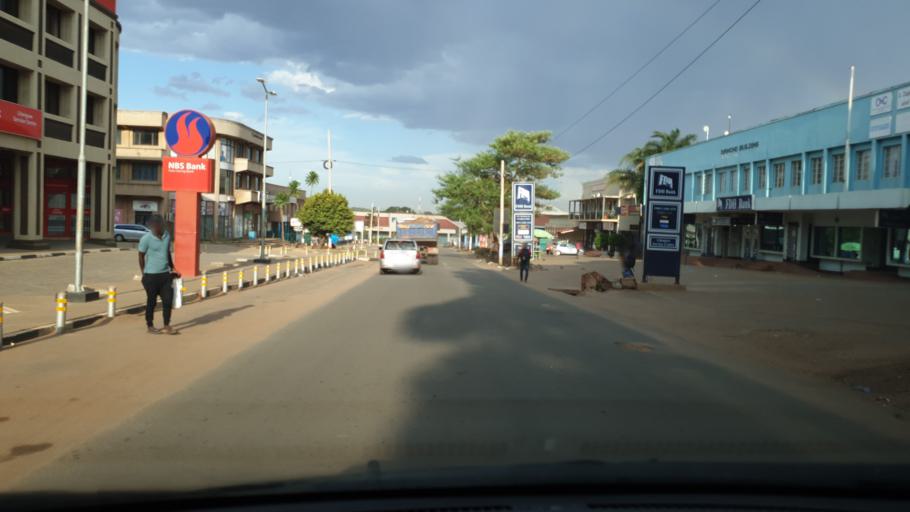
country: MW
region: Central Region
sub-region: Lilongwe District
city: Lilongwe
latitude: -13.9878
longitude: 33.7668
